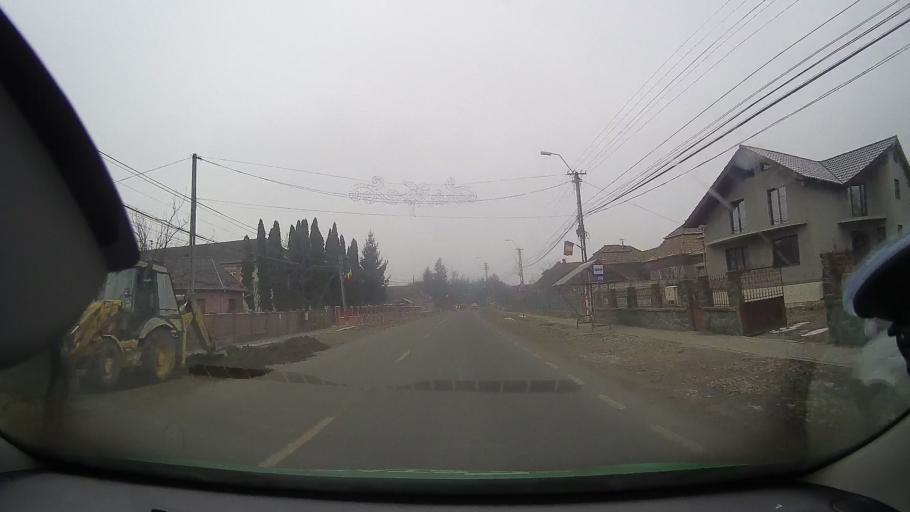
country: RO
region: Cluj
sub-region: Comuna Mihai Viteazu
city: Mihai Viteazu
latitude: 46.5407
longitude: 23.7478
